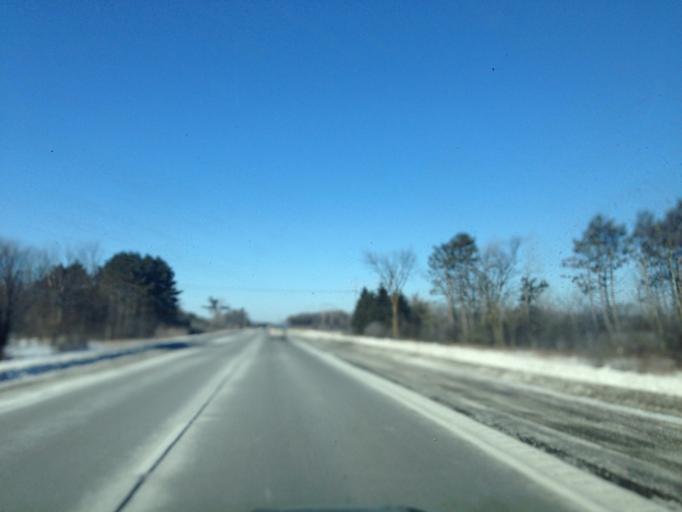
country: CA
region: Ontario
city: Ottawa
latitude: 45.3717
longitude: -75.5521
